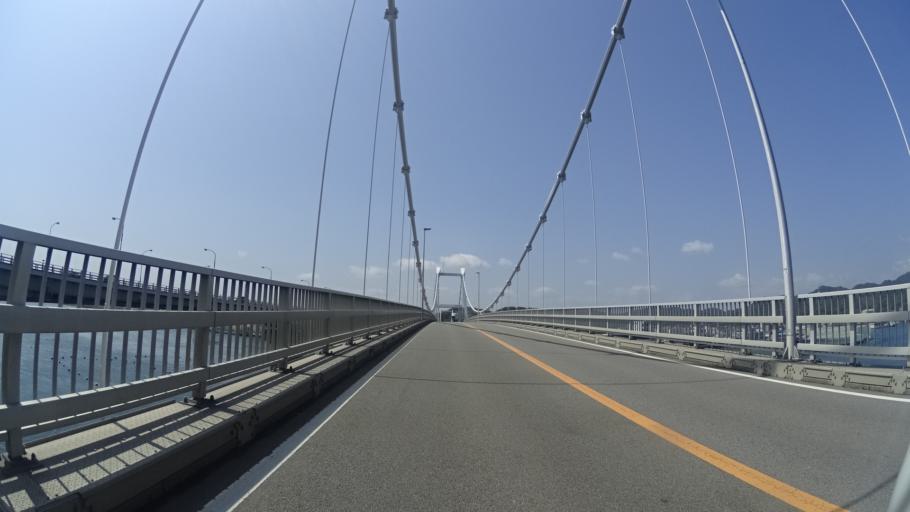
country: JP
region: Tokushima
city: Narutocho-mitsuishi
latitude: 34.1933
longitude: 134.6124
